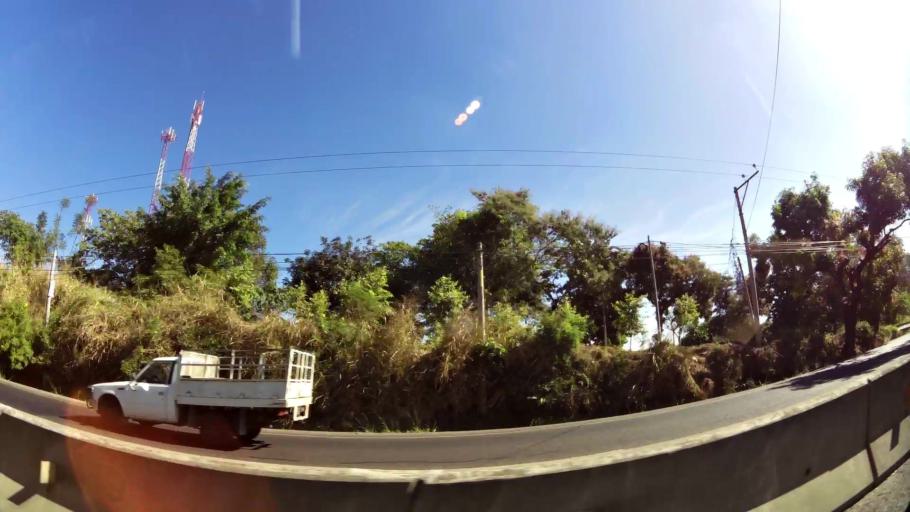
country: SV
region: Santa Ana
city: Coatepeque
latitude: 13.9355
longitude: -89.5252
